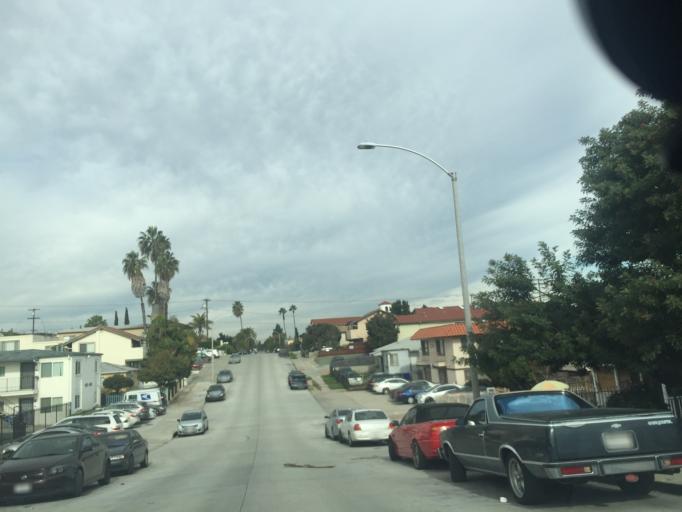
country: US
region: California
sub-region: San Diego County
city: Lemon Grove
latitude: 32.7502
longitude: -117.0912
